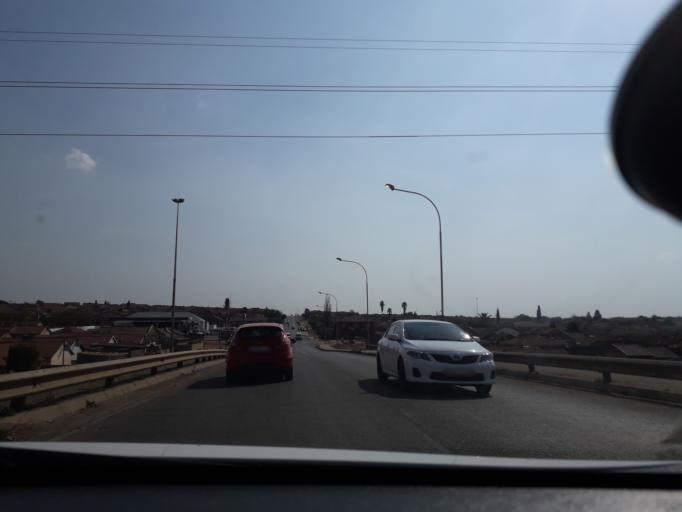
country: ZA
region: Gauteng
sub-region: Ekurhuleni Metropolitan Municipality
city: Tembisa
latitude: -25.9904
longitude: 28.2463
